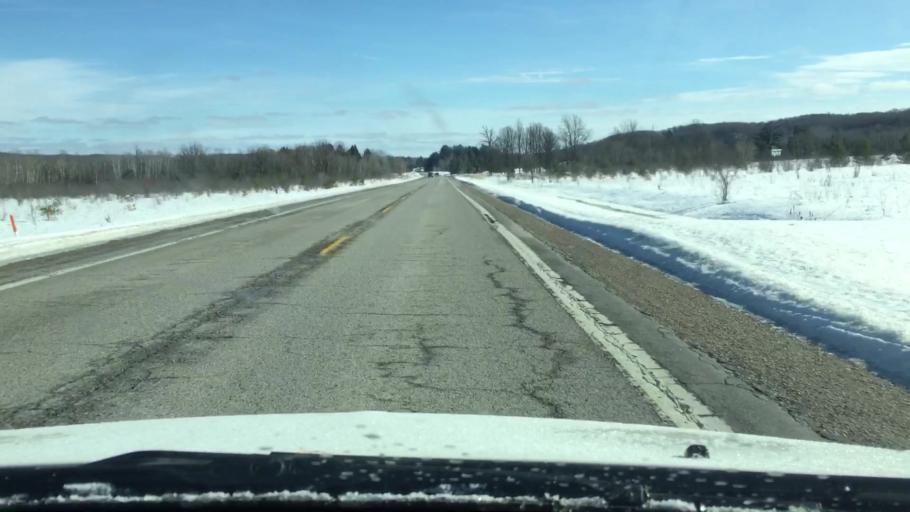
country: US
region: Michigan
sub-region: Charlevoix County
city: East Jordan
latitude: 45.1025
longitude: -85.1178
